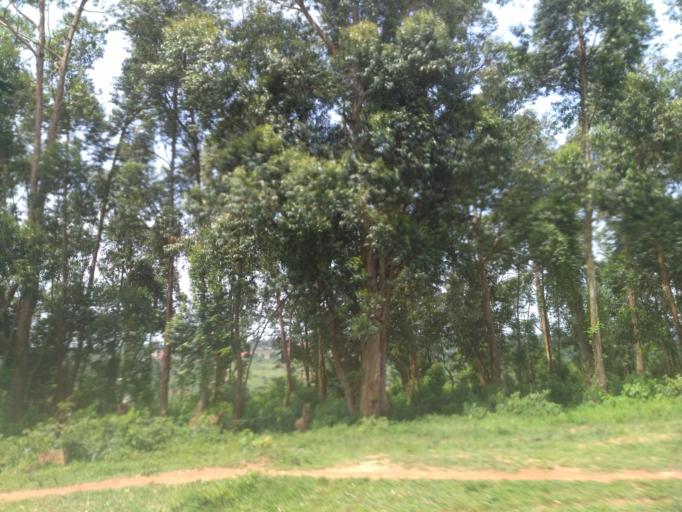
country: UG
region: Central Region
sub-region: Wakiso District
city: Kireka
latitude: 0.4646
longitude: 32.6057
